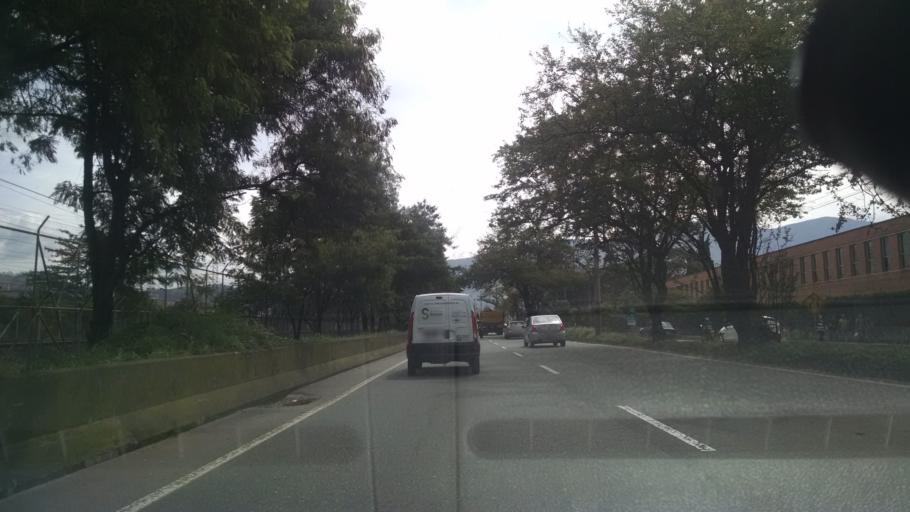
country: CO
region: Antioquia
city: Envigado
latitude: 6.1732
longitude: -75.5995
